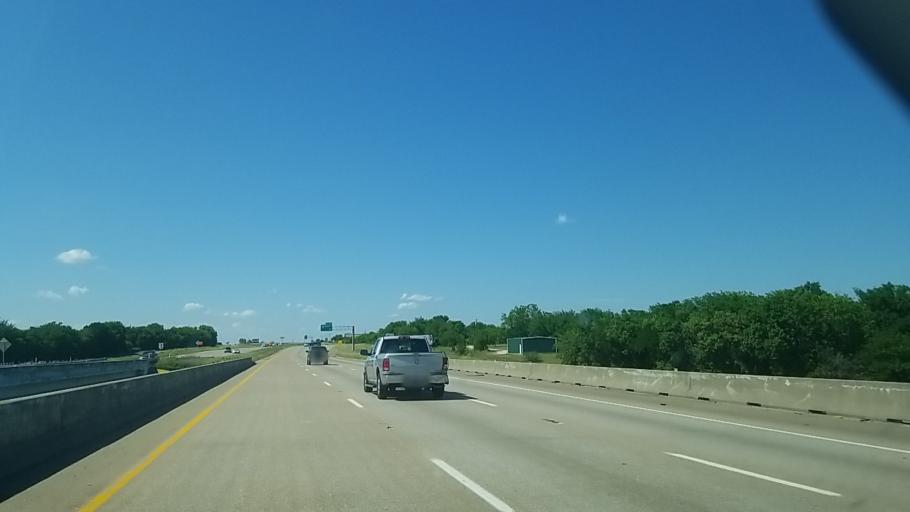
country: US
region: Texas
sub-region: Ellis County
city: Ferris
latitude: 32.5057
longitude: -96.6636
